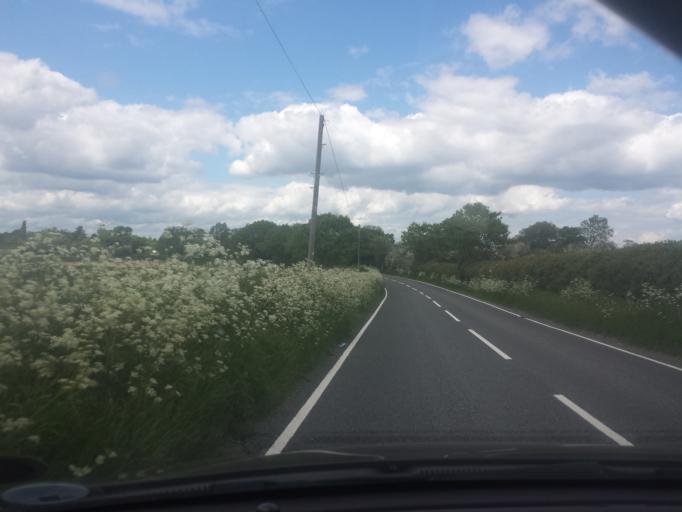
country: GB
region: England
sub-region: Essex
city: Little Clacton
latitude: 51.8290
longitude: 1.1592
